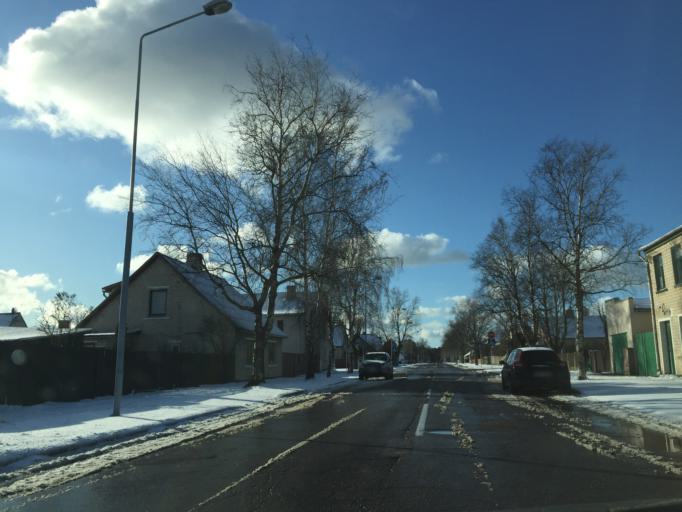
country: LV
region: Ventspils
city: Ventspils
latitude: 57.3856
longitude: 21.5572
